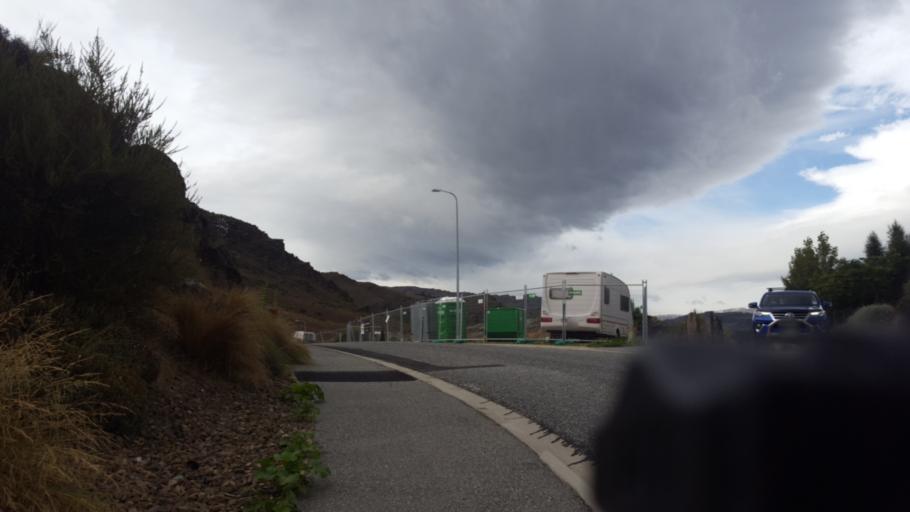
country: NZ
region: Otago
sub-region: Queenstown-Lakes District
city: Wanaka
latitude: -45.2521
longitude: 169.4027
